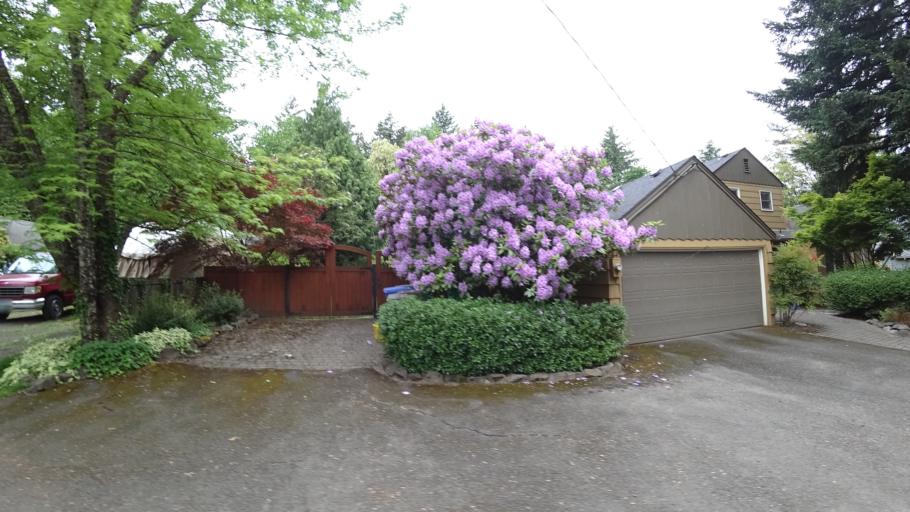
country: US
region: Oregon
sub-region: Washington County
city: Garden Home-Whitford
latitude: 45.4633
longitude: -122.7324
